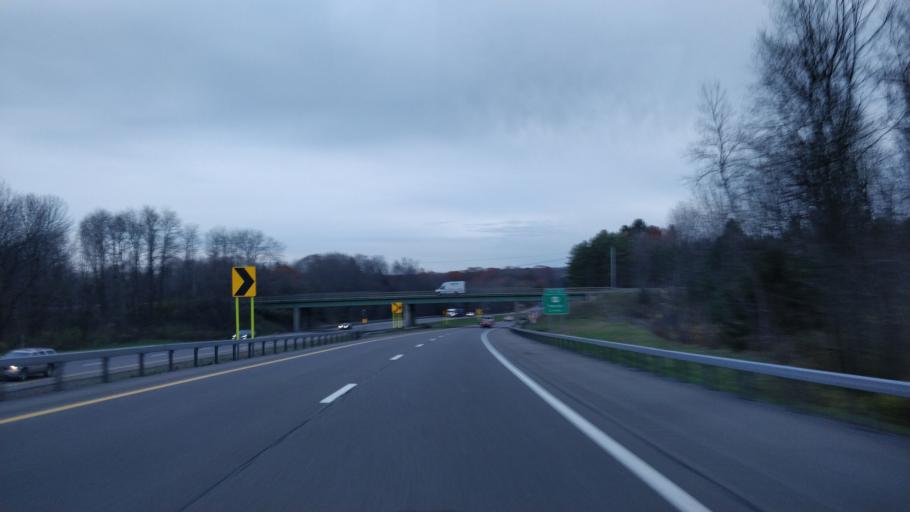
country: US
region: New York
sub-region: Oswego County
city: Central Square
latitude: 43.3721
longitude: -76.1220
